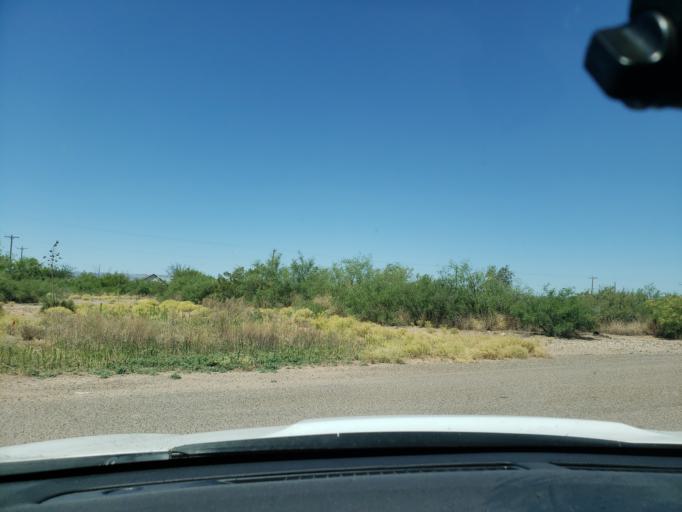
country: US
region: Texas
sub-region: Presidio County
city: Marfa
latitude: 30.5849
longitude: -104.4911
